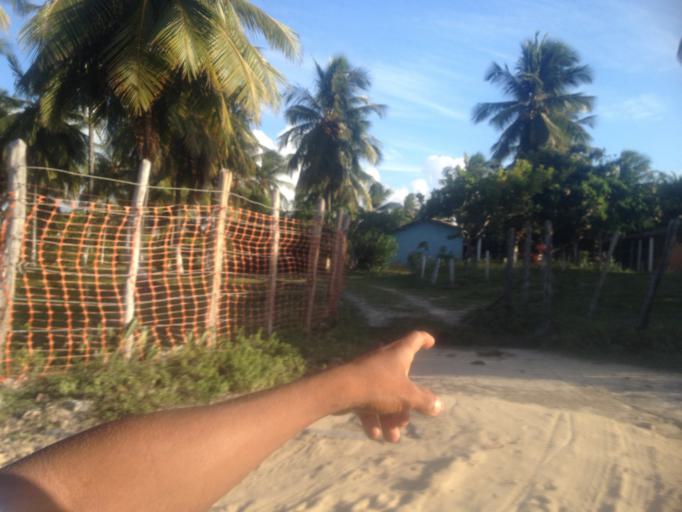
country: BR
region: Sergipe
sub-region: Indiaroba
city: Indiaroba
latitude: -11.4641
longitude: -37.3608
